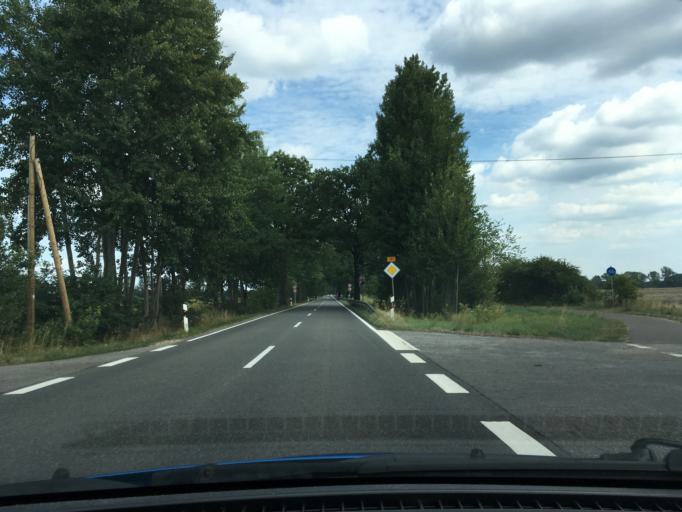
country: DE
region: Mecklenburg-Vorpommern
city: Eldena
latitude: 53.2720
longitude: 11.4583
